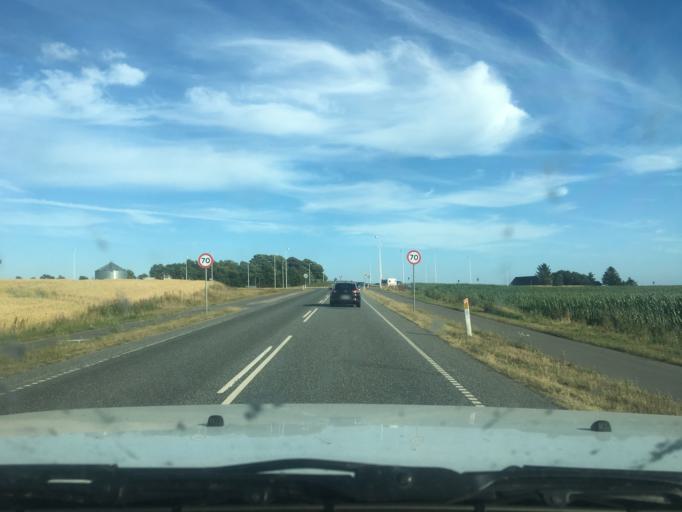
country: DK
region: Central Jutland
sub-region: Syddjurs Kommune
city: Hornslet
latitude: 56.3549
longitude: 10.3443
